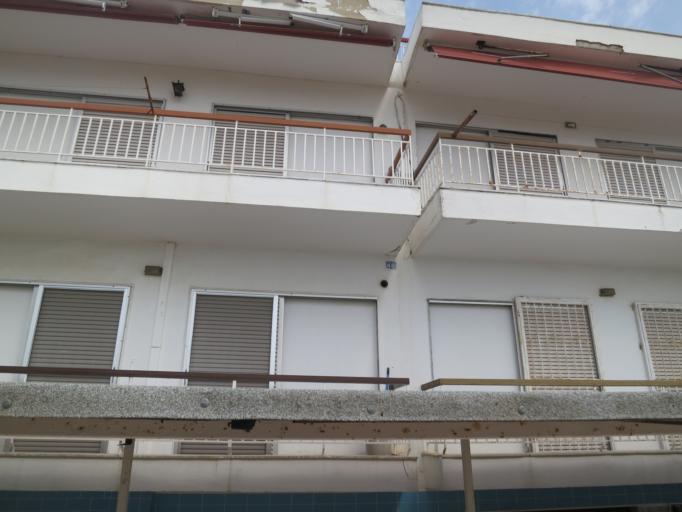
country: GR
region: Central Macedonia
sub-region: Nomos Chalkidikis
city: Nea Moudhania
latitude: 40.2489
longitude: 23.2531
